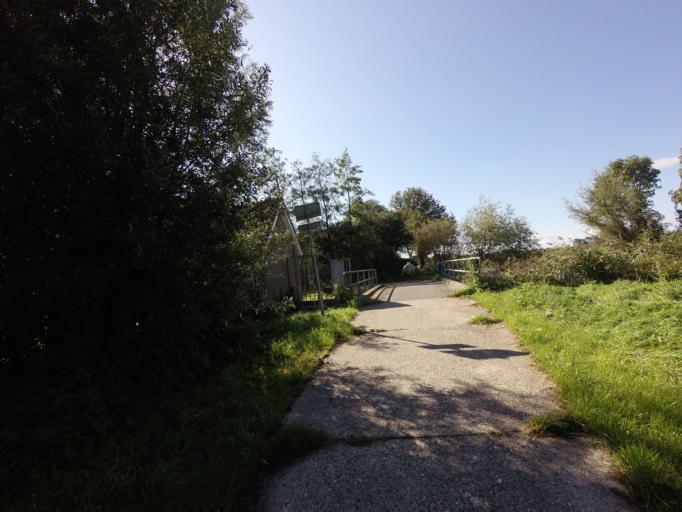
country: NL
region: Friesland
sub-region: Gemeente Leeuwarden
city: Wirdum
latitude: 53.1570
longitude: 5.7657
